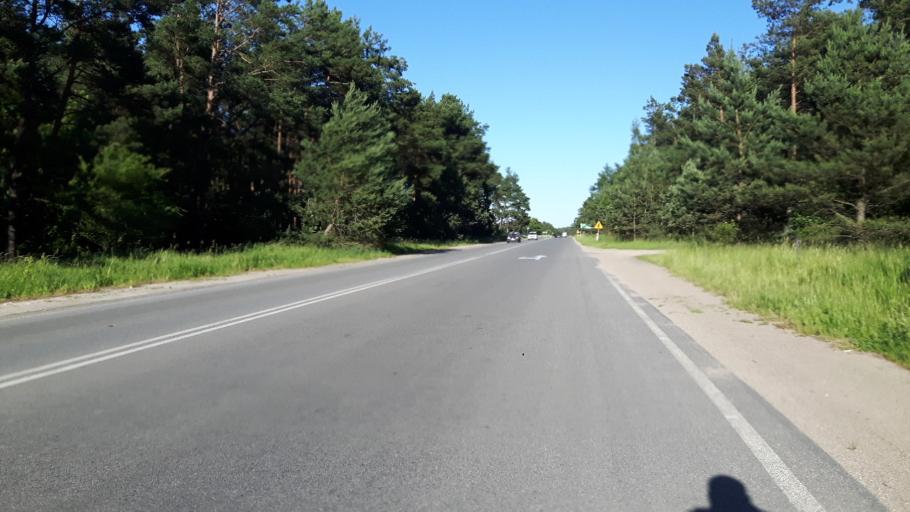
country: PL
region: Pomeranian Voivodeship
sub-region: Powiat pucki
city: Kosakowo
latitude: 54.6048
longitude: 18.4497
